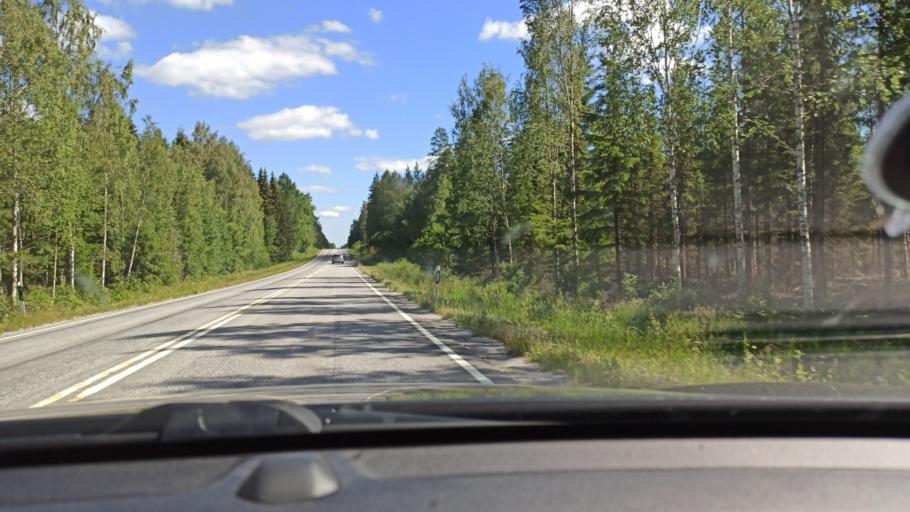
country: FI
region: Ostrobothnia
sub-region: Vaasa
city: Malax
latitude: 62.9862
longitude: 21.6331
